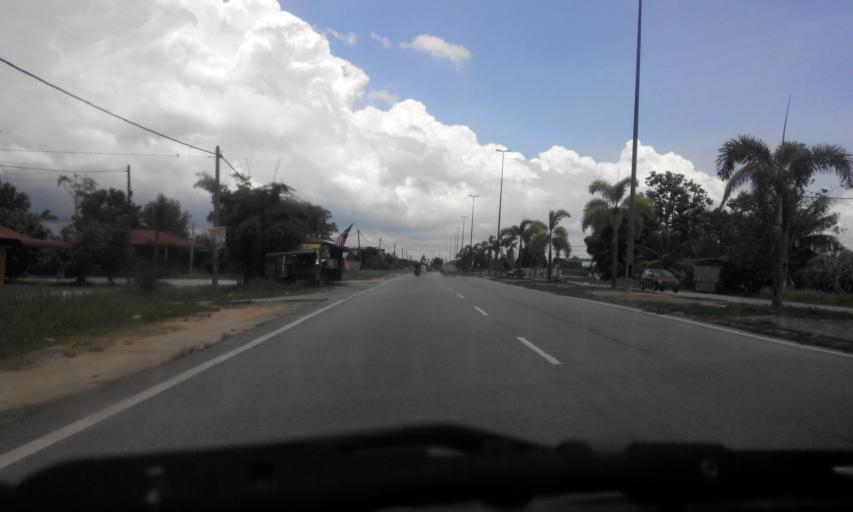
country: MY
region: Perak
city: Parit Buntar
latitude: 5.1304
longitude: 100.4996
